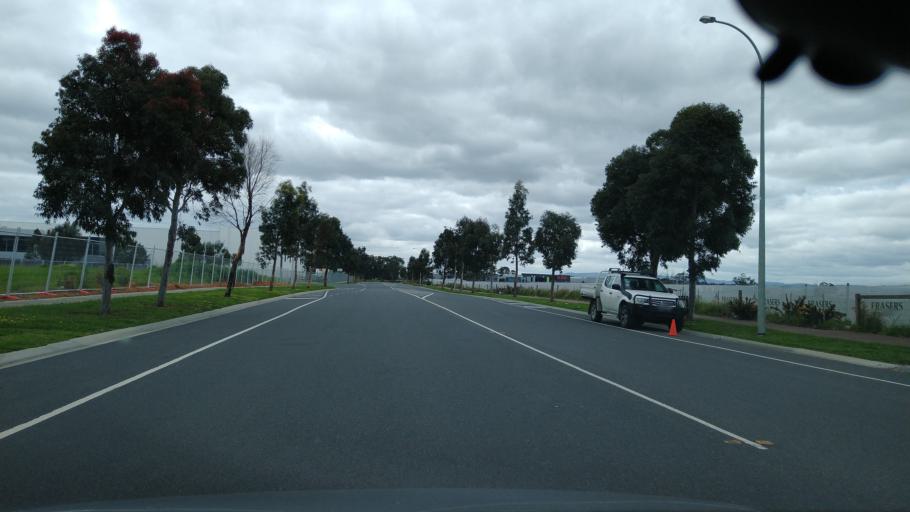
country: AU
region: Victoria
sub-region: Frankston
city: Sandhurst
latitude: -38.0503
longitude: 145.2166
